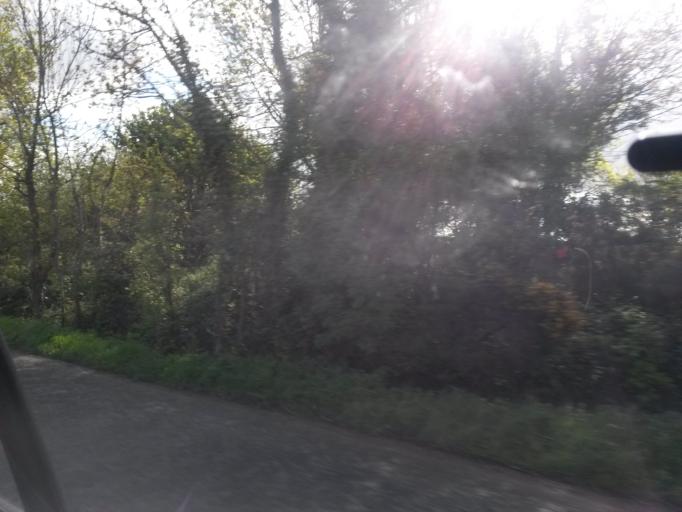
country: IE
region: Leinster
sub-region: Loch Garman
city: Ferns
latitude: 52.5669
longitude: -6.5249
